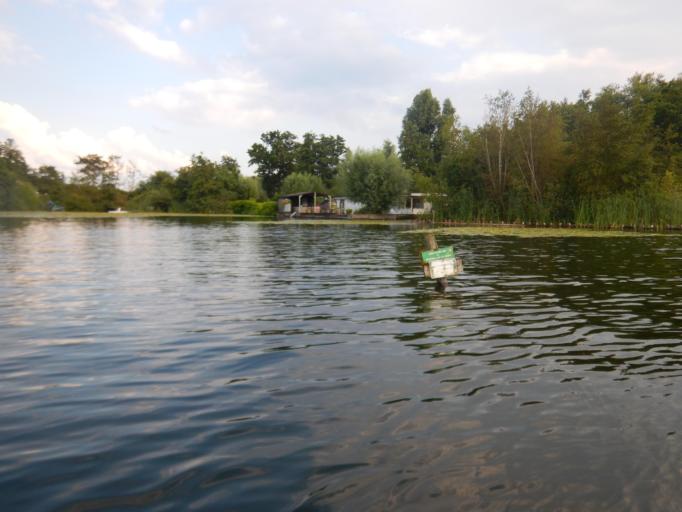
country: NL
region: North Holland
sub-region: Gemeente Wijdemeren
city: Oud-Loosdrecht
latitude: 52.2213
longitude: 5.0678
